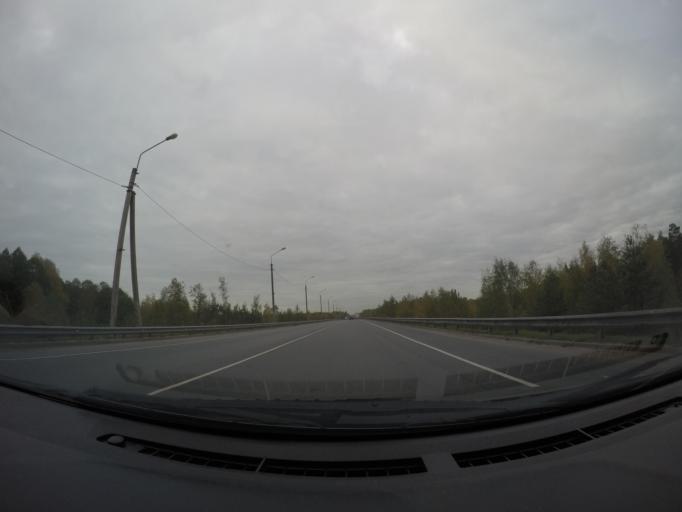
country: RU
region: Moskovskaya
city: Fryazevo
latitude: 55.7207
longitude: 38.4190
